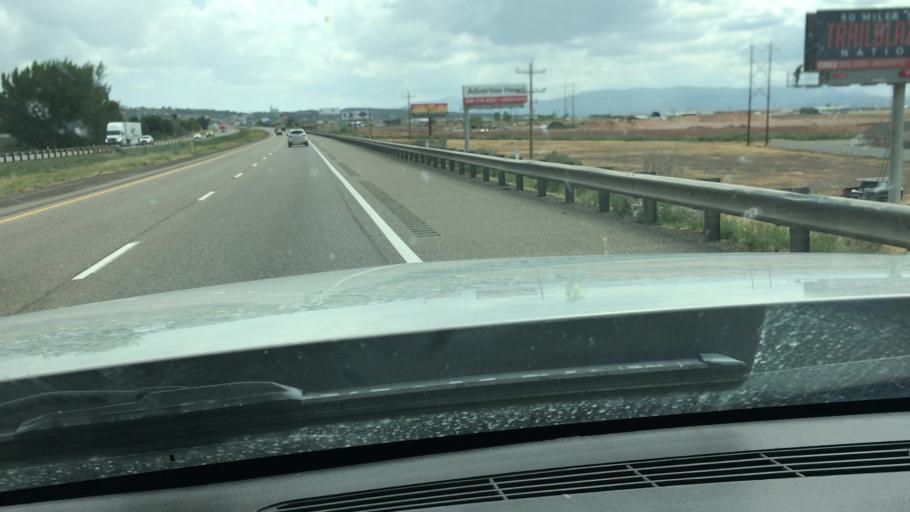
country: US
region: Utah
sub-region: Iron County
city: Cedar City
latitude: 37.7118
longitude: -113.0677
